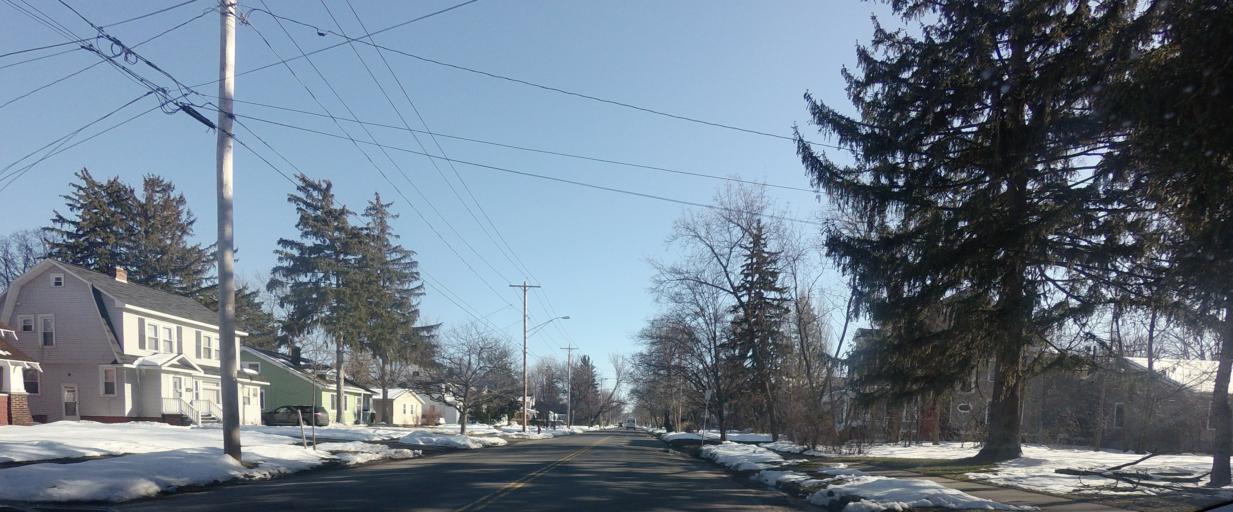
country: US
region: New York
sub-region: Onondaga County
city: Nedrow
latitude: 43.0051
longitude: -76.1473
